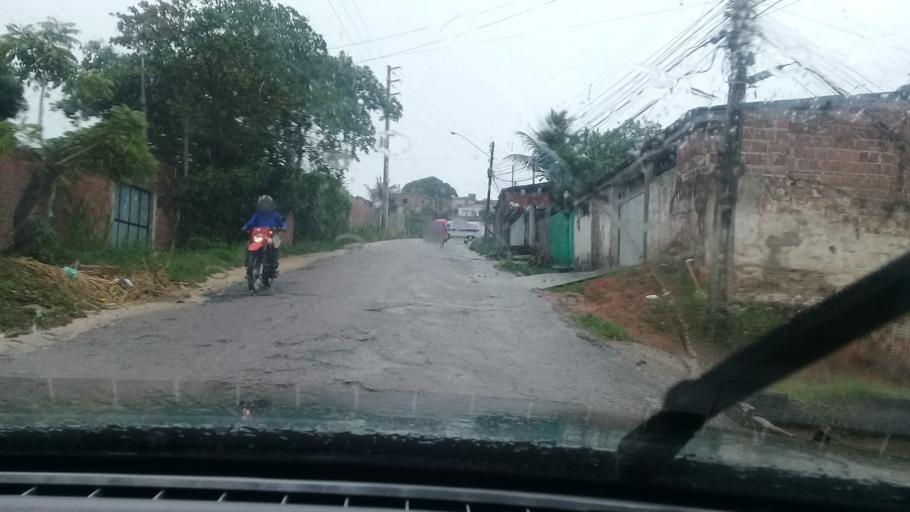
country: BR
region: Pernambuco
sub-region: Paulista
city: Paulista
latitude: -7.9516
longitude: -34.8891
